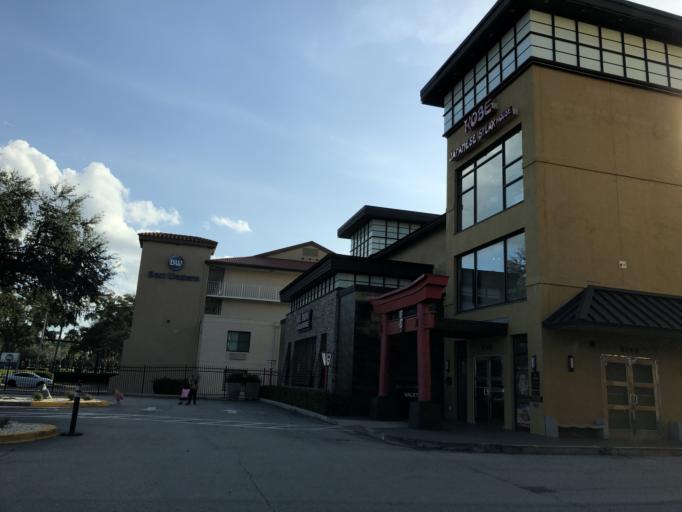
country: US
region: Florida
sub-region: Orange County
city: Doctor Phillips
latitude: 28.4480
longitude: -81.4714
